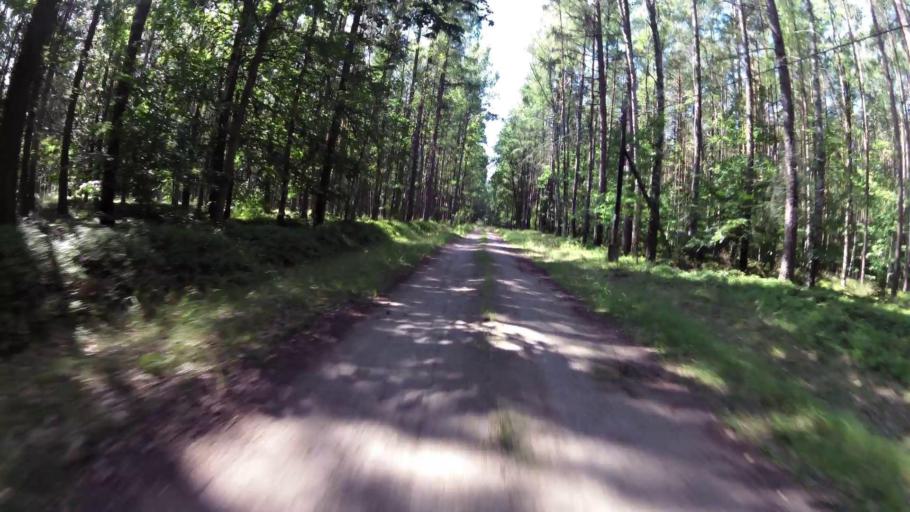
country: PL
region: West Pomeranian Voivodeship
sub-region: Powiat drawski
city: Czaplinek
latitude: 53.4241
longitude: 16.2655
